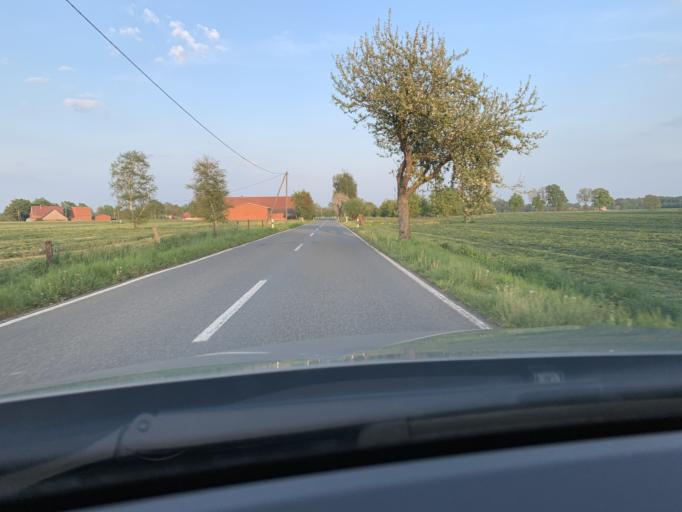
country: DE
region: North Rhine-Westphalia
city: Rietberg
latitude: 51.7963
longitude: 8.3917
